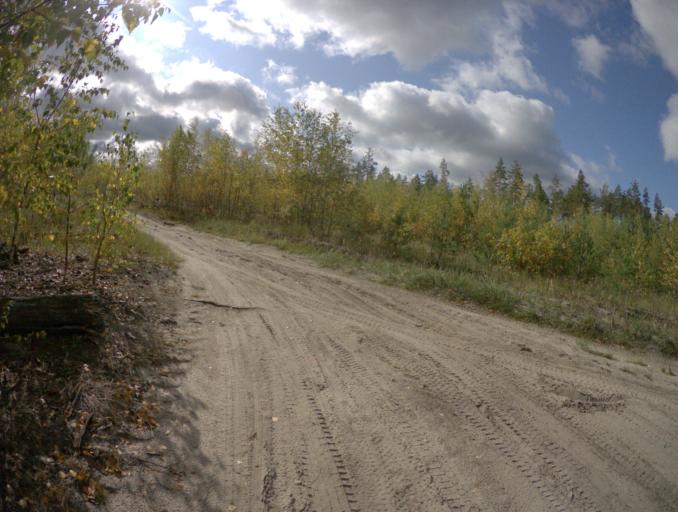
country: RU
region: Moskovskaya
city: Baksheyevo
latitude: 55.7348
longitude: 39.8193
